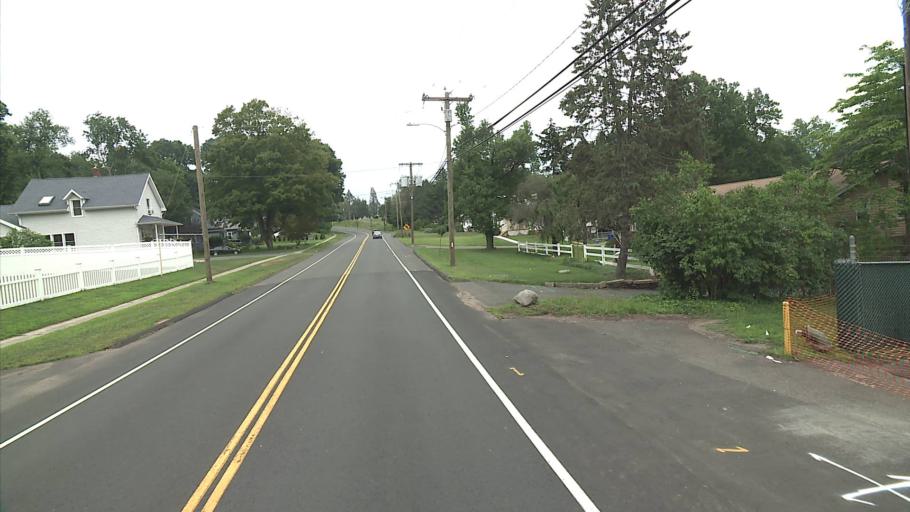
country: US
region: Connecticut
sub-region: Hartford County
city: Wethersfield
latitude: 41.6572
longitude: -72.6399
